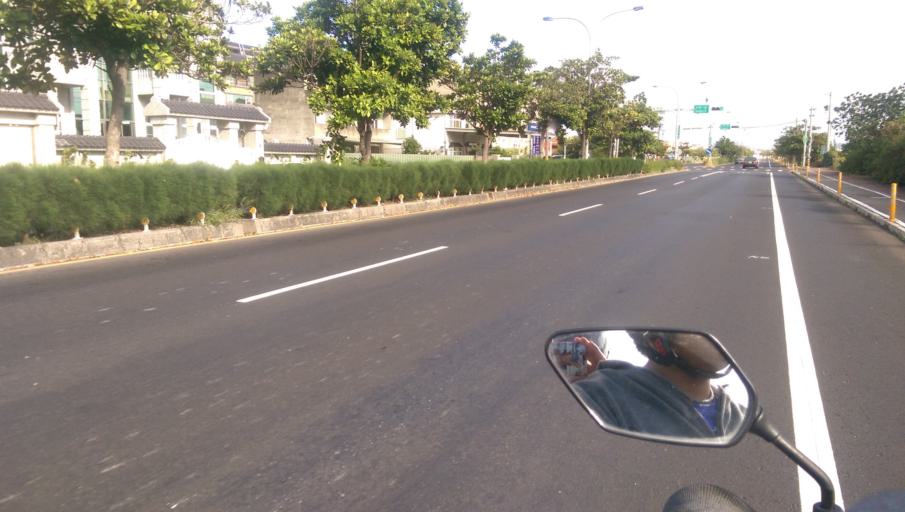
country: TW
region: Taiwan
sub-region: Hsinchu
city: Hsinchu
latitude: 24.8381
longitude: 120.9363
